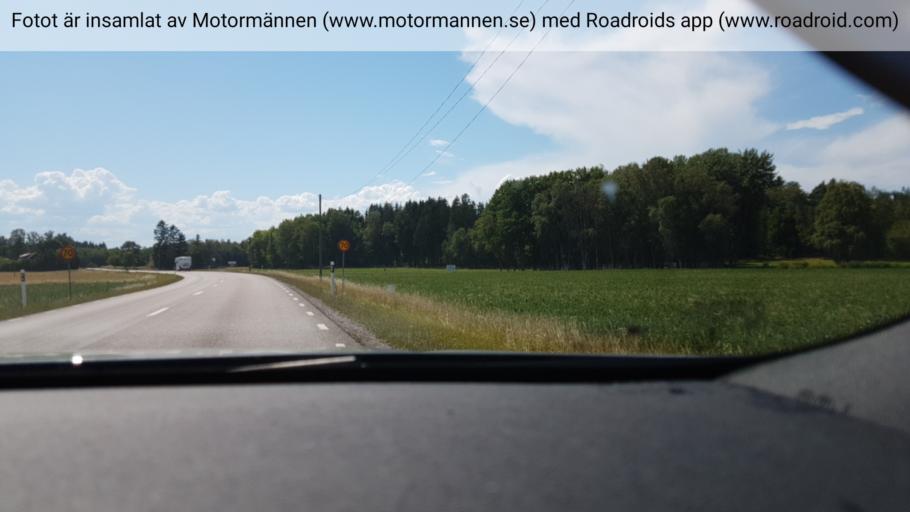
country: SE
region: Vaestra Goetaland
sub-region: Grastorps Kommun
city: Graestorp
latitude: 58.3904
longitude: 12.7666
